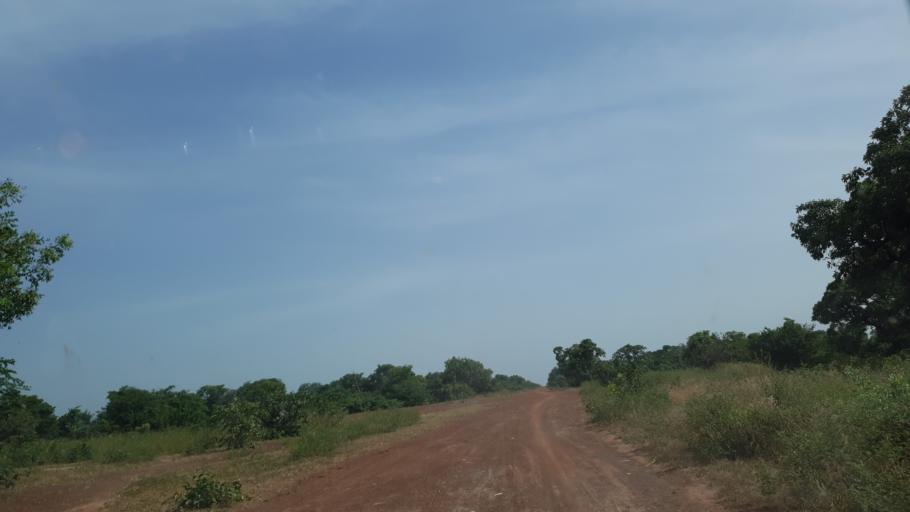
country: ML
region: Koulikoro
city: Dioila
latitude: 12.4324
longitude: -6.2159
